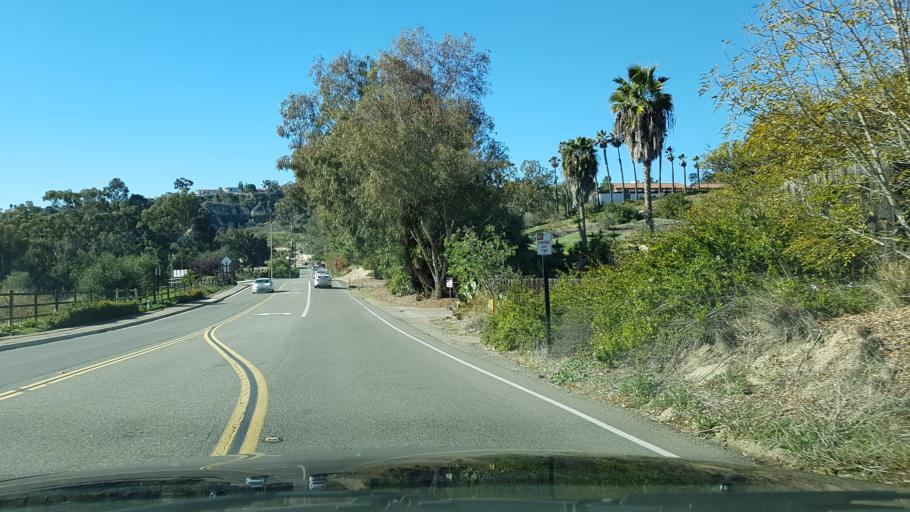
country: US
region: California
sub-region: San Diego County
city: Solana Beach
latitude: 33.0218
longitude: -117.2517
